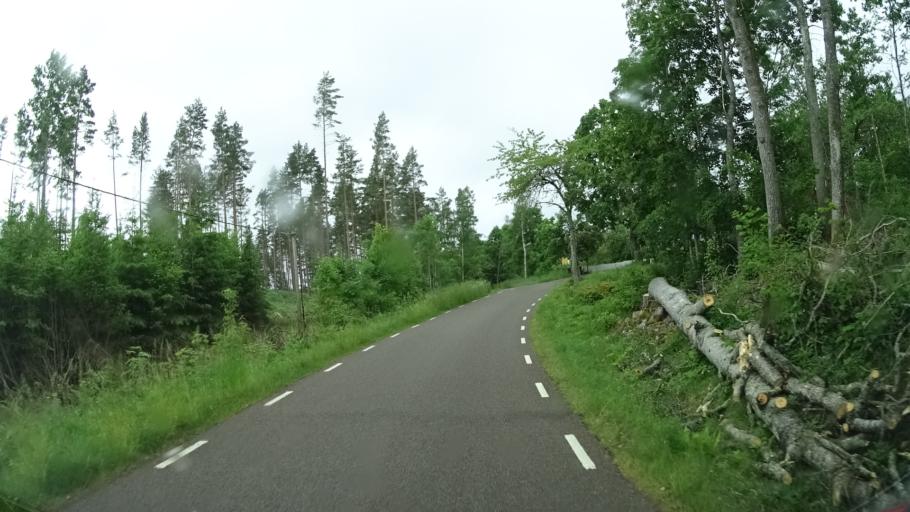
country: SE
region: Kalmar
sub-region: Vimmerby Kommun
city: Sodra Vi
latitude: 57.7056
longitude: 15.7553
